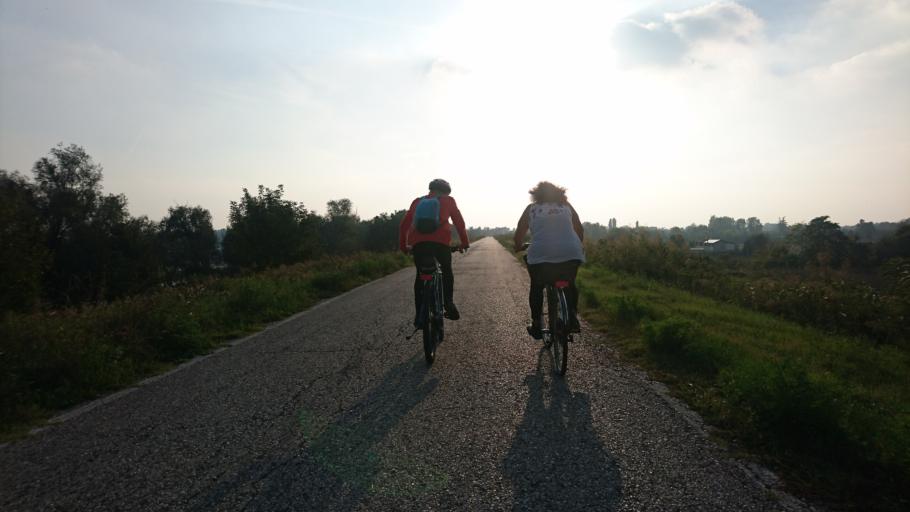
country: IT
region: Veneto
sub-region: Provincia di Rovigo
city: Canaro
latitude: 44.9232
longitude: 11.6978
